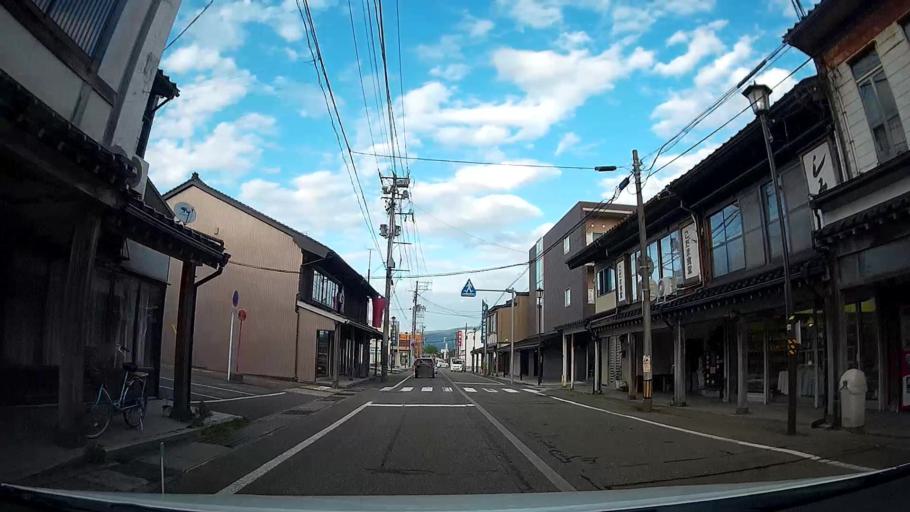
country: JP
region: Niigata
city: Itoigawa
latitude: 37.0449
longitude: 137.8575
